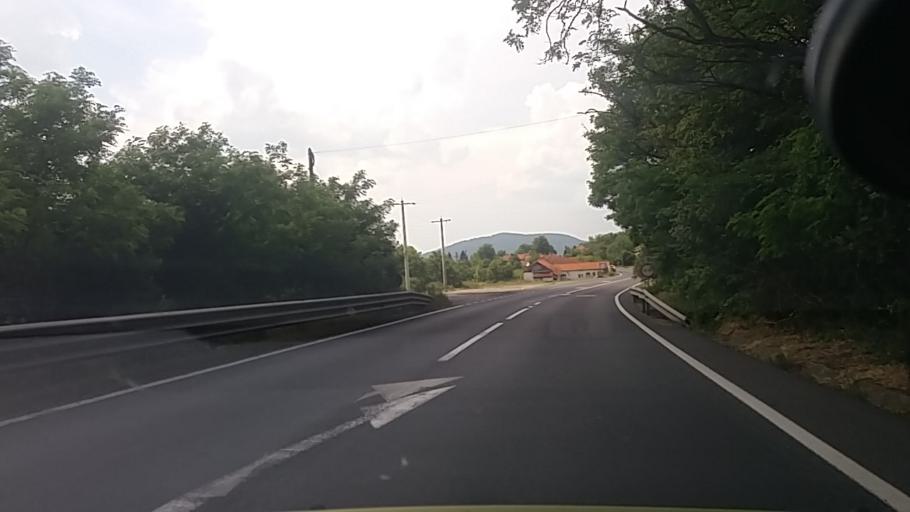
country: RO
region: Hunedoara
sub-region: Comuna Burjuc
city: Burjuc
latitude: 45.9454
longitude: 22.4952
